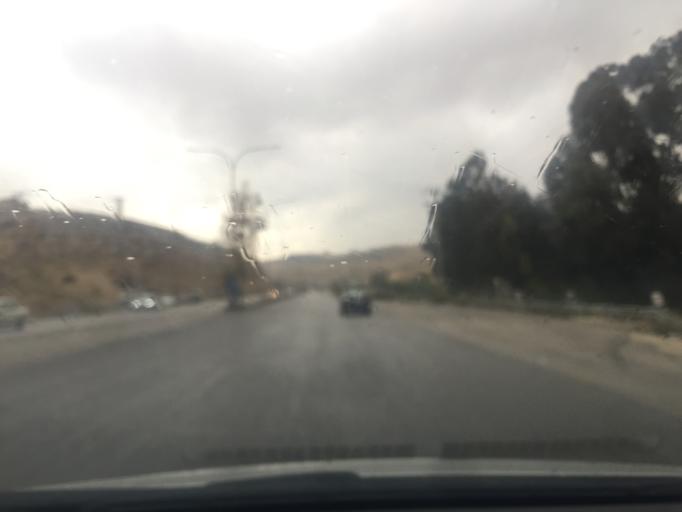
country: JO
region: Zarqa
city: Russeifa
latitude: 32.0184
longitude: 35.9900
